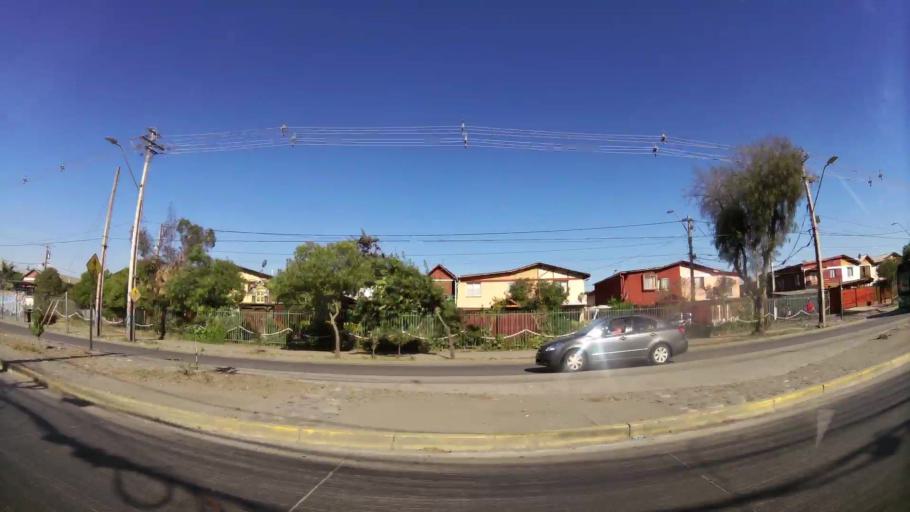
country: CL
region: Santiago Metropolitan
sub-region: Provincia de Maipo
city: San Bernardo
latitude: -33.5897
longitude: -70.6787
